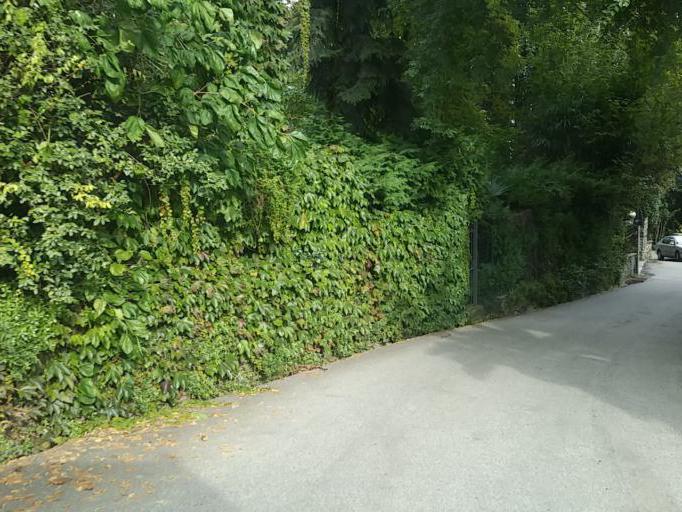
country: IT
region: Piedmont
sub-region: Provincia Verbano-Cusio-Ossola
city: Gonte
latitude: 45.9976
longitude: 8.6542
